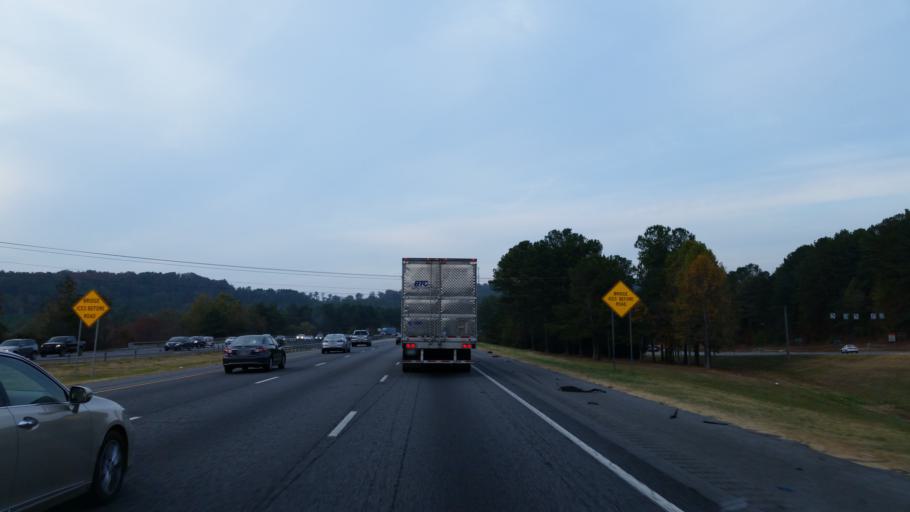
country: US
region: Georgia
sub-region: Bartow County
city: Cartersville
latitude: 34.2048
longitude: -84.7614
